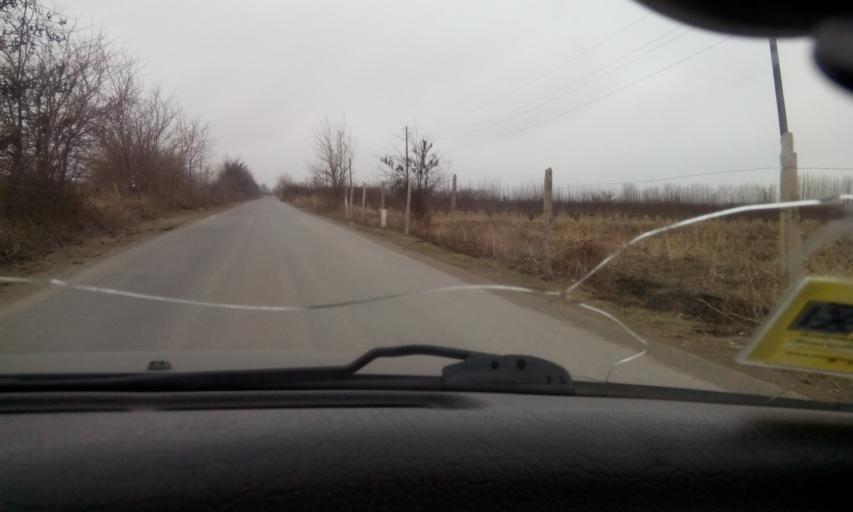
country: AM
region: Armavir
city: Lukashin
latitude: 40.1785
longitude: 43.9811
